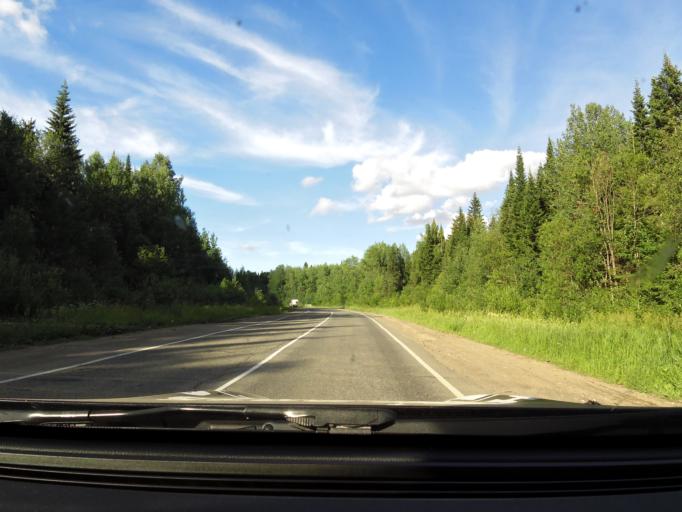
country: RU
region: Kirov
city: Omutninsk
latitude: 58.7004
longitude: 52.2385
